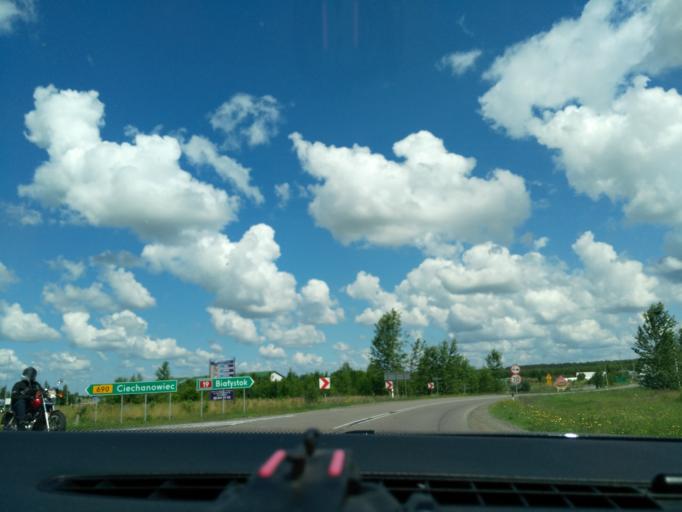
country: PL
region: Podlasie
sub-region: Powiat siemiatycki
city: Siemiatycze
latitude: 52.4411
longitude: 22.8506
